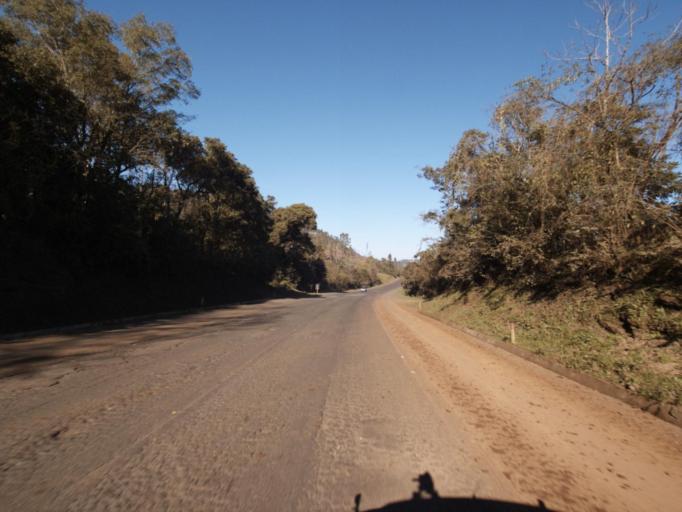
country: BR
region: Rio Grande do Sul
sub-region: Frederico Westphalen
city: Frederico Westphalen
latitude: -26.9596
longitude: -53.2054
